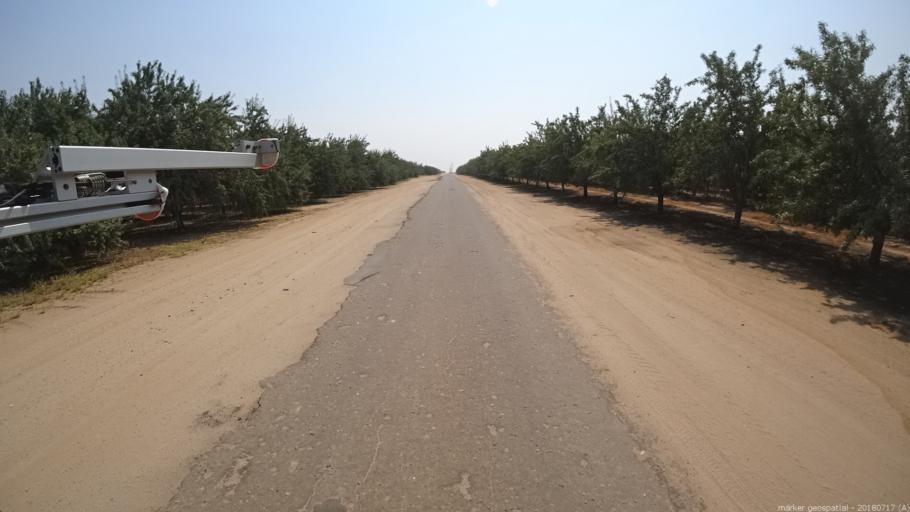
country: US
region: California
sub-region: Madera County
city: Fairmead
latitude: 37.1486
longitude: -120.1286
